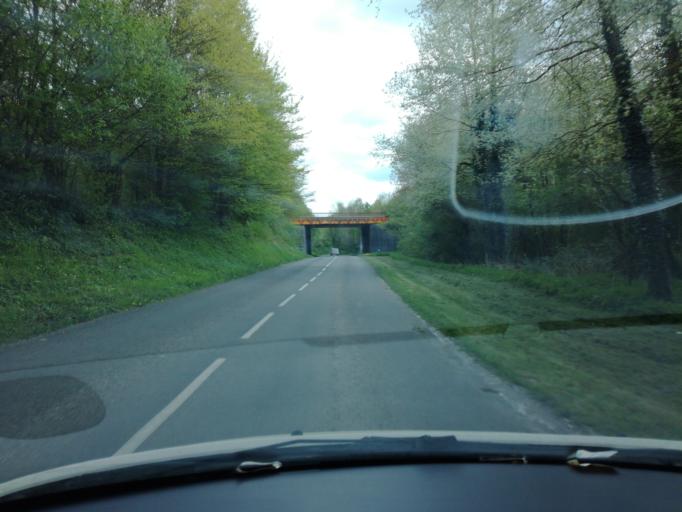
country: FR
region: Picardie
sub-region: Departement de la Somme
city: Poix-de-Picardie
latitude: 49.7853
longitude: 1.9903
